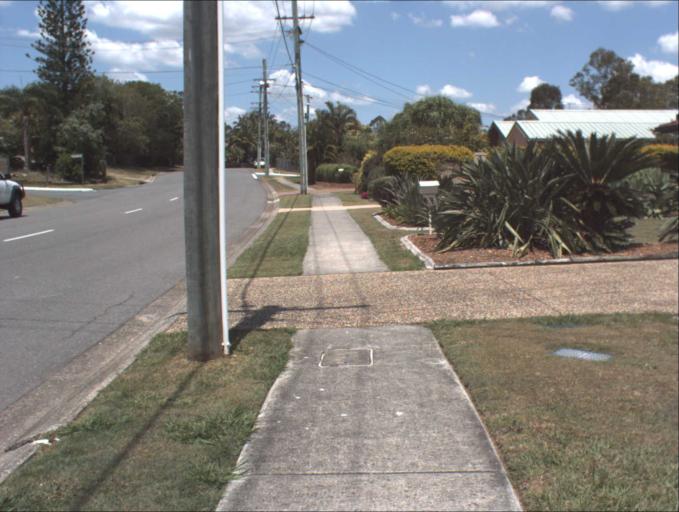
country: AU
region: Queensland
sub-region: Logan
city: Springwood
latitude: -27.6029
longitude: 153.1394
